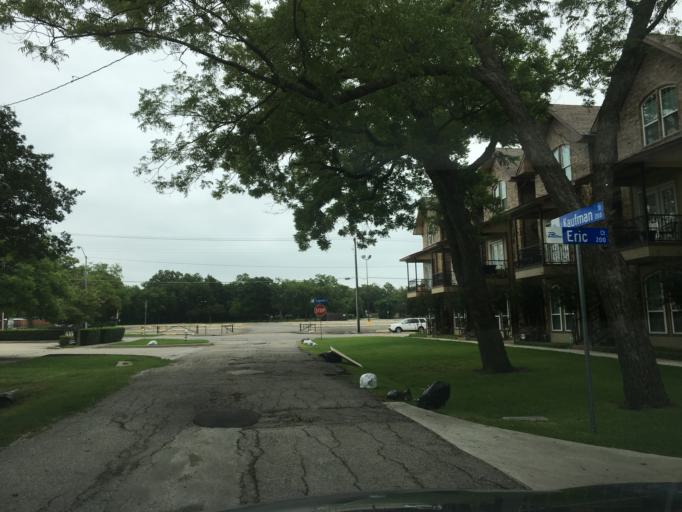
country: US
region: Texas
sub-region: Dallas County
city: Richardson
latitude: 32.9470
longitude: -96.7315
